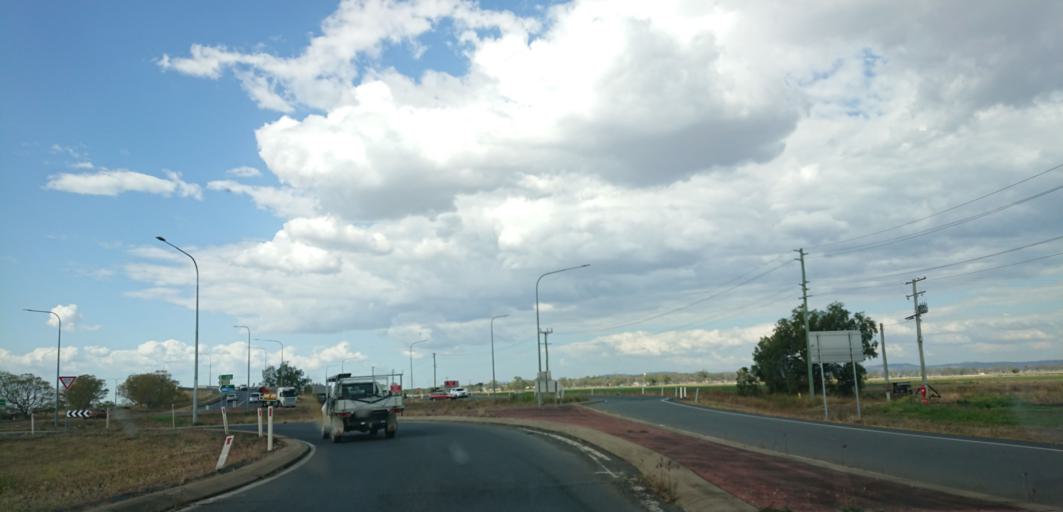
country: AU
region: Queensland
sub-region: Lockyer Valley
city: Gatton
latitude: -27.5501
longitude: 152.3142
